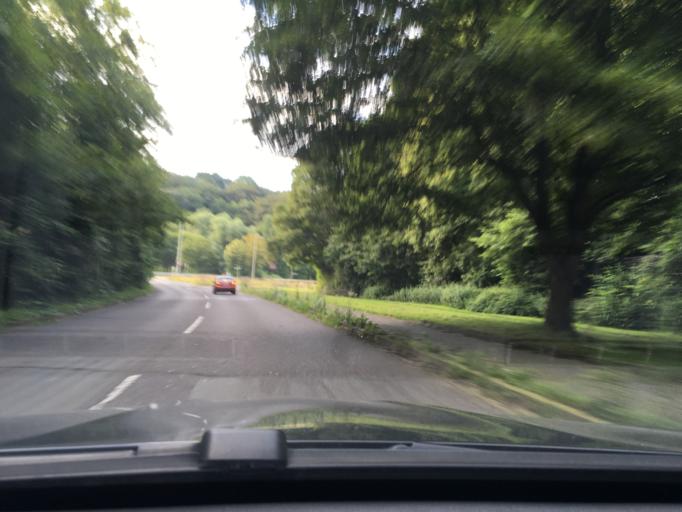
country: DE
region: North Rhine-Westphalia
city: Opladen
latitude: 51.0447
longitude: 7.0594
